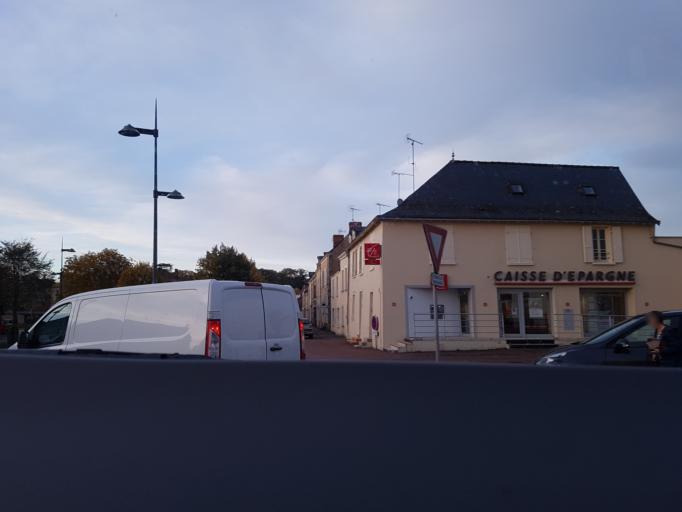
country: FR
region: Pays de la Loire
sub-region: Departement de la Mayenne
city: Craon
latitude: 47.8471
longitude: -0.9481
